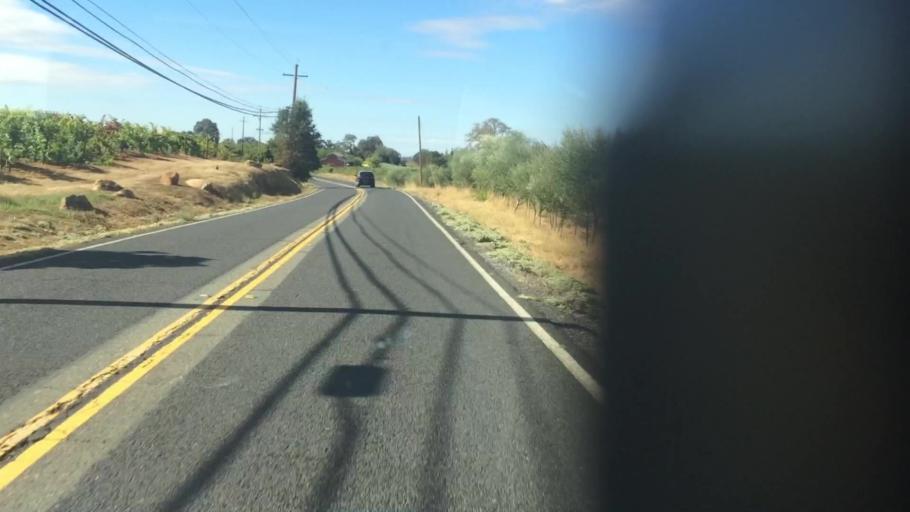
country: US
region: California
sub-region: Amador County
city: Plymouth
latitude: 38.5242
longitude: -120.8177
